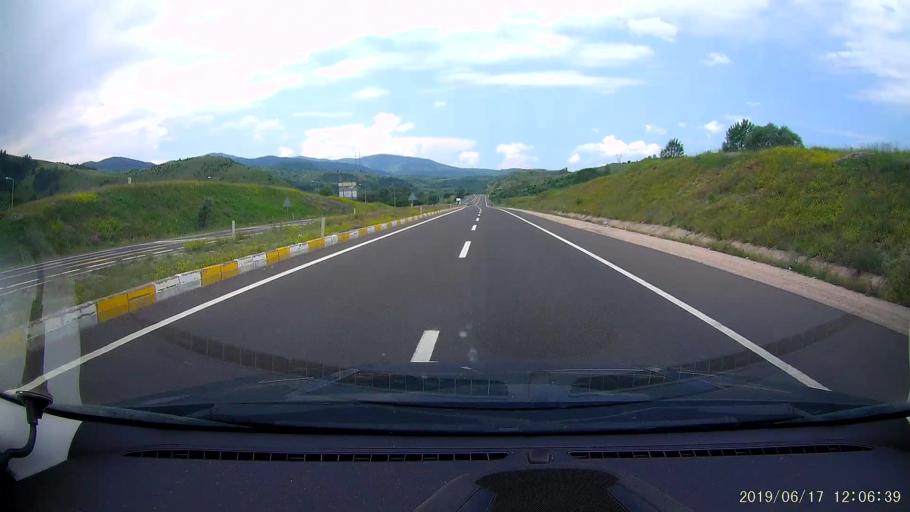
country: TR
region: Cankiri
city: Cerkes
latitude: 40.8398
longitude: 32.7534
